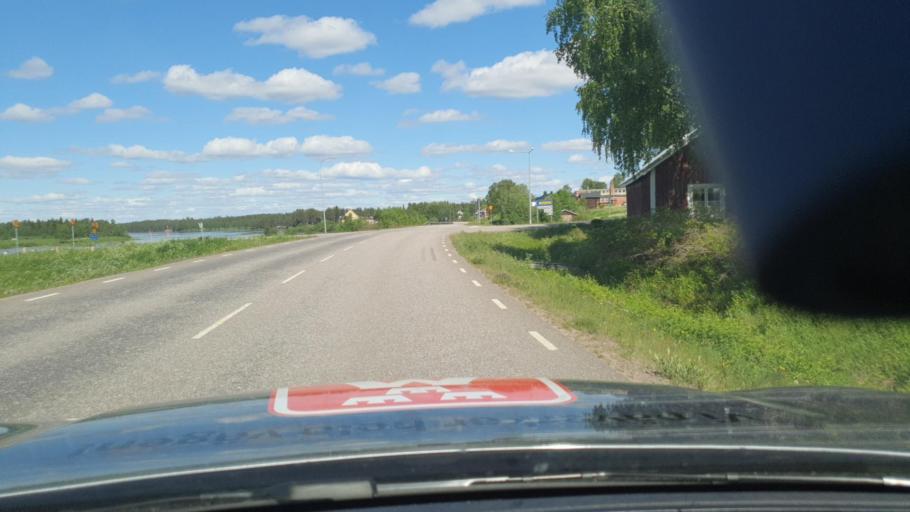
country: SE
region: Norrbotten
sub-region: Pajala Kommun
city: Pajala
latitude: 67.1673
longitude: 22.6148
